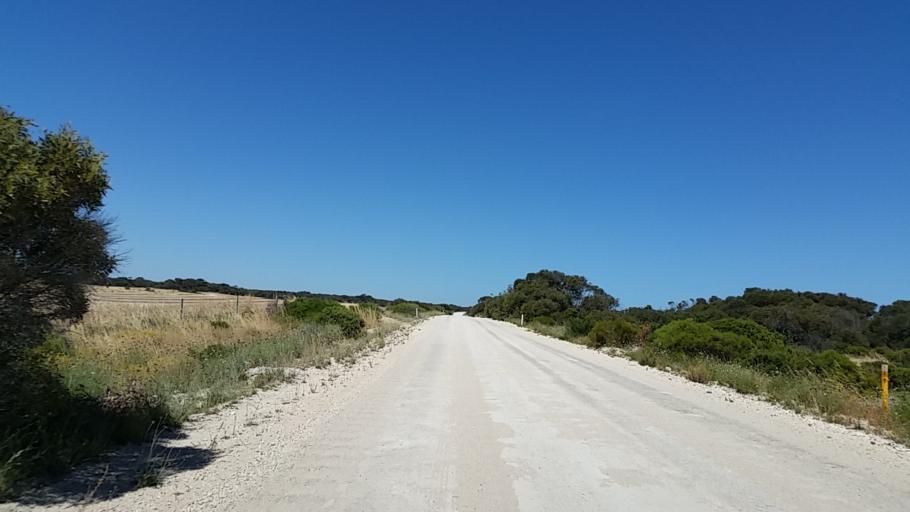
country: AU
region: South Australia
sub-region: Yorke Peninsula
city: Honiton
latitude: -35.2215
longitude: 137.0752
